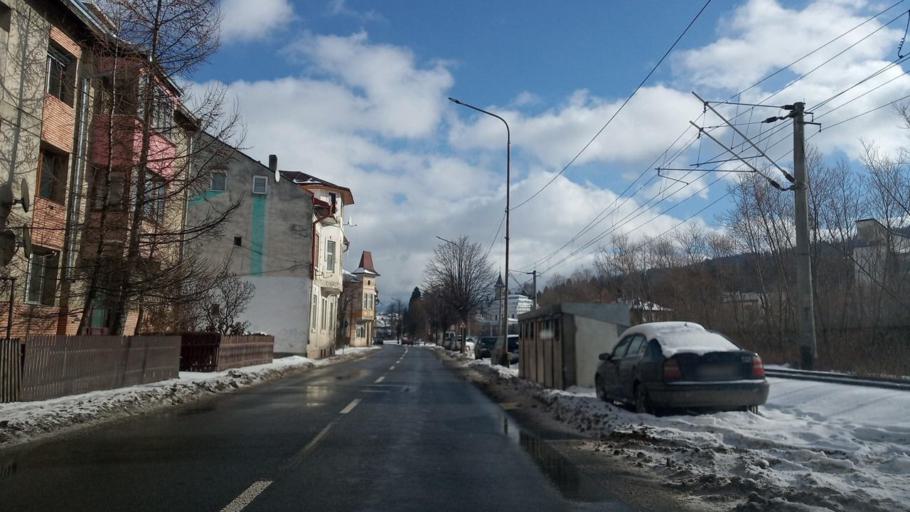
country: RO
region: Suceava
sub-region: Municipiul Vatra Dornei
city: Vatra Dornei
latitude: 47.3463
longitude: 25.3516
